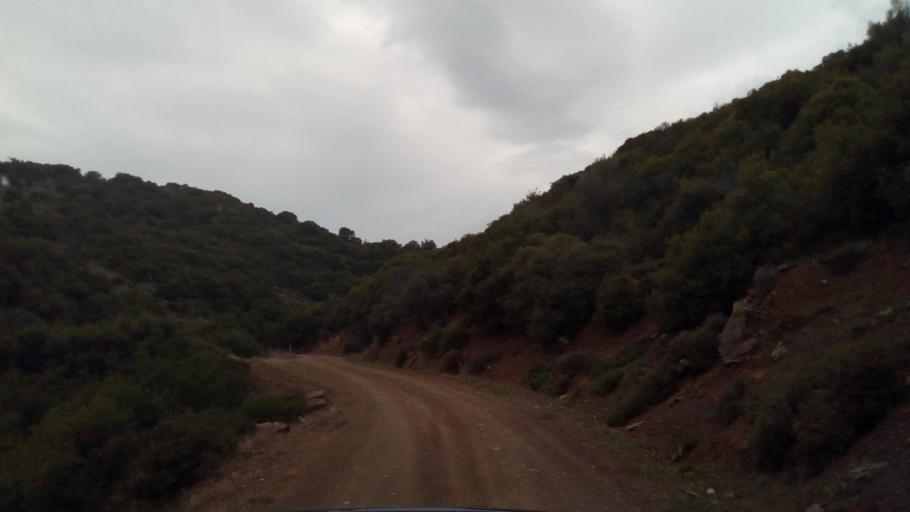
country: GR
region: West Greece
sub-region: Nomos Achaias
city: Aigio
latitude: 38.3768
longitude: 22.1541
